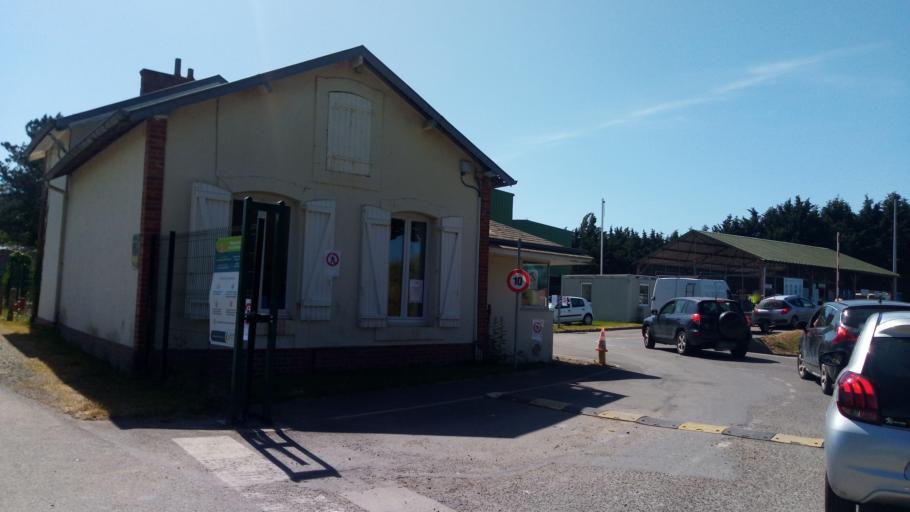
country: FR
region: Lower Normandy
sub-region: Departement de la Manche
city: Saint-Pair-sur-Mer
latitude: 48.8250
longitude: -1.5504
